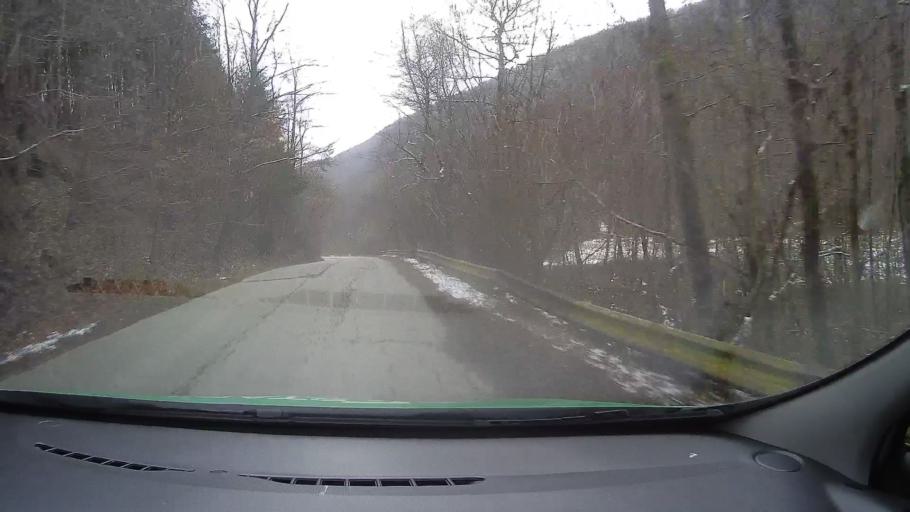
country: RO
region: Hunedoara
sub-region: Comuna Balsa
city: Balsa
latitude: 45.9999
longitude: 23.1503
